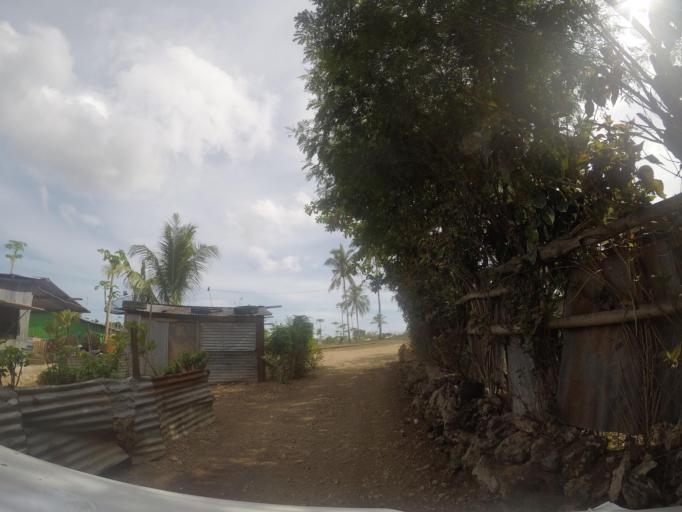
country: TL
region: Baucau
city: Baucau
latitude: -8.4825
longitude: 126.4547
